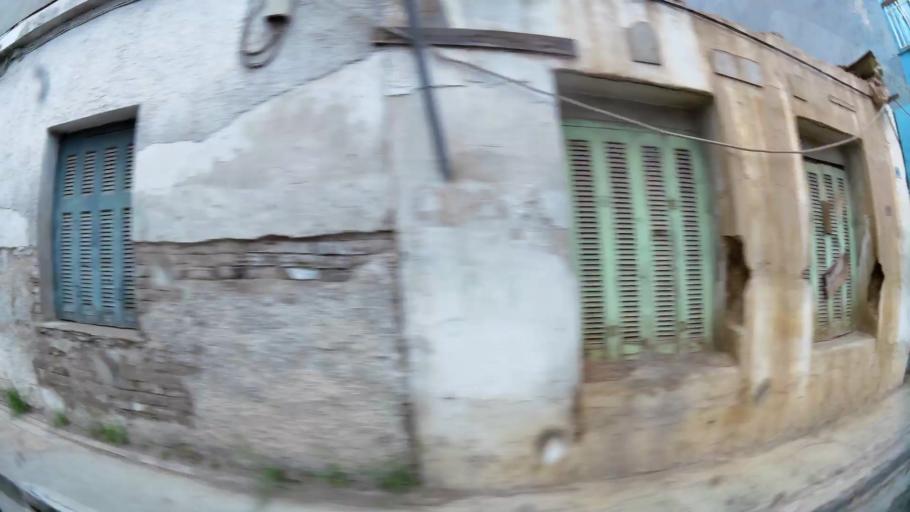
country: GR
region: Attica
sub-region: Nomarchia Athinas
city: Aigaleo
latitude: 37.9827
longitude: 23.6869
